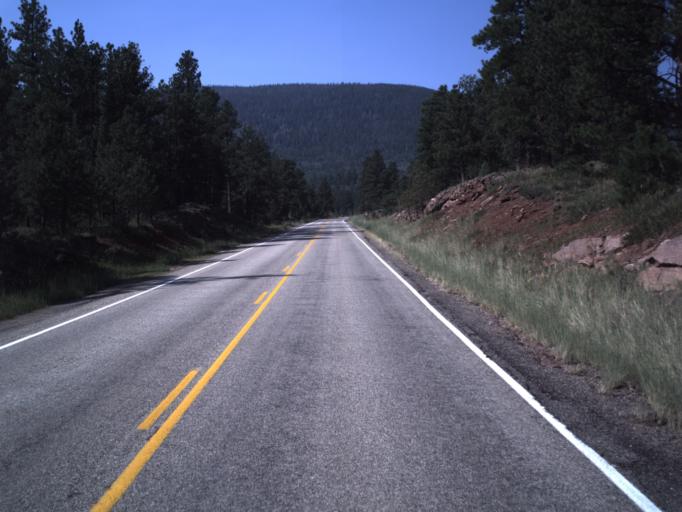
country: US
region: Utah
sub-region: Daggett County
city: Manila
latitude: 40.8683
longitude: -109.4737
